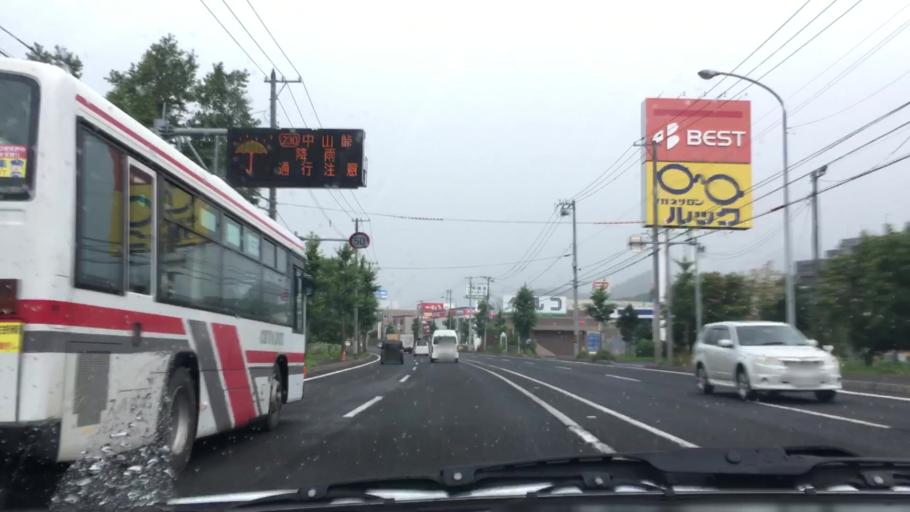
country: JP
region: Hokkaido
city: Sapporo
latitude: 42.9911
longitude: 141.3345
